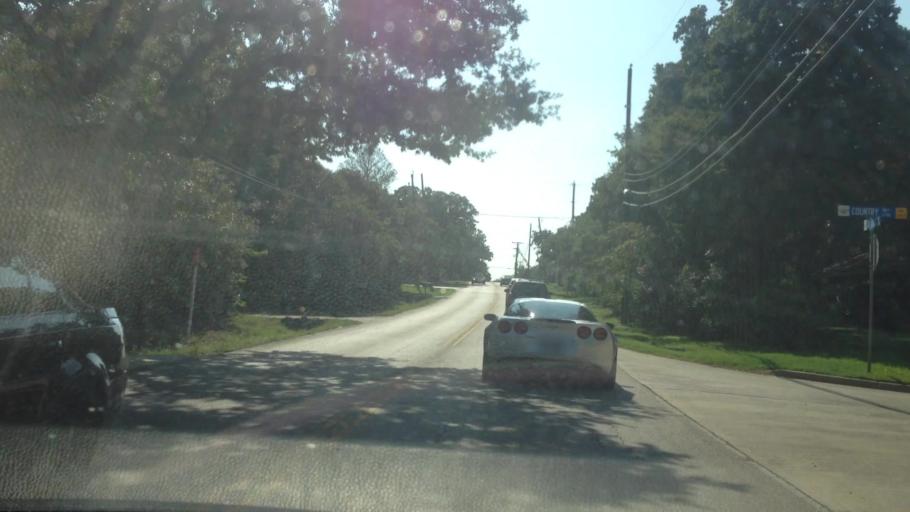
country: US
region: Texas
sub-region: Tarrant County
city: Colleyville
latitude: 32.8927
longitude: -97.1761
